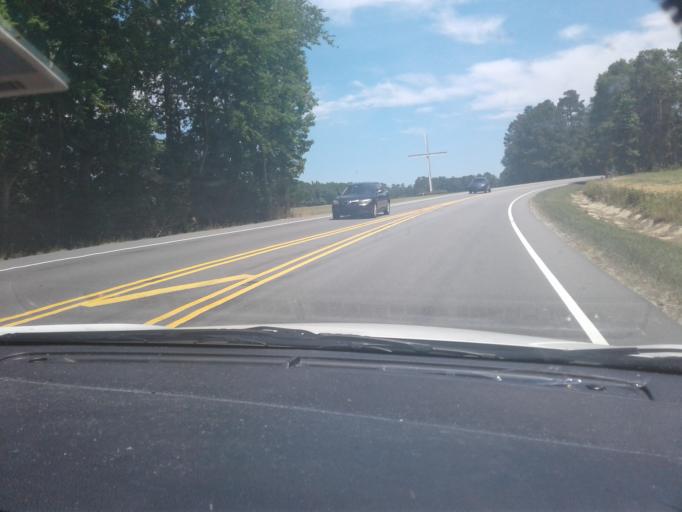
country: US
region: North Carolina
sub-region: Harnett County
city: Lillington
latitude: 35.4738
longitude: -78.8266
